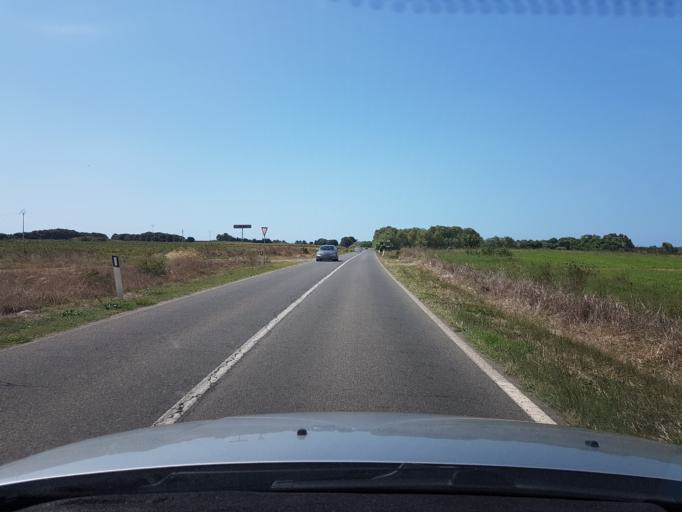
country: IT
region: Sardinia
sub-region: Provincia di Oristano
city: Riola Sardo
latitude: 40.0208
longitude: 8.4830
